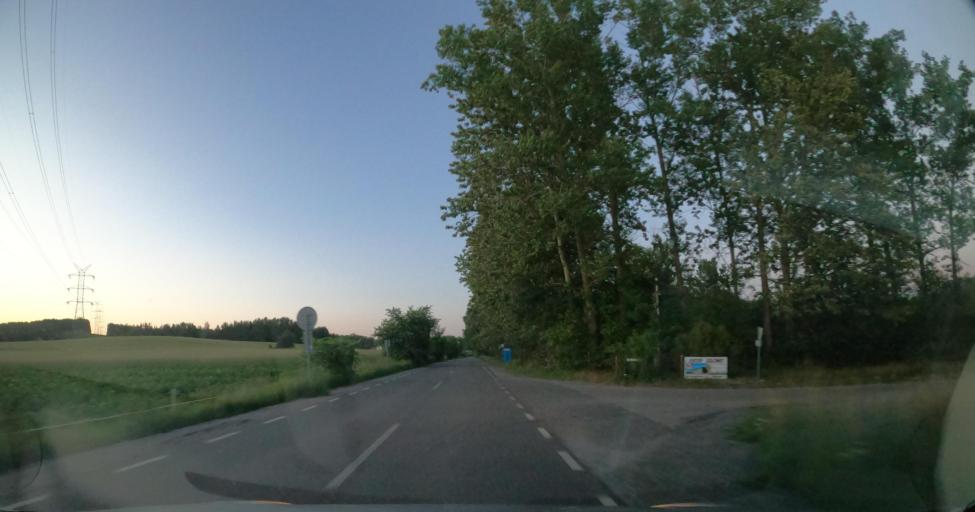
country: PL
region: Pomeranian Voivodeship
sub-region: Powiat wejherowski
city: Szemud
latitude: 54.4743
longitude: 18.1758
